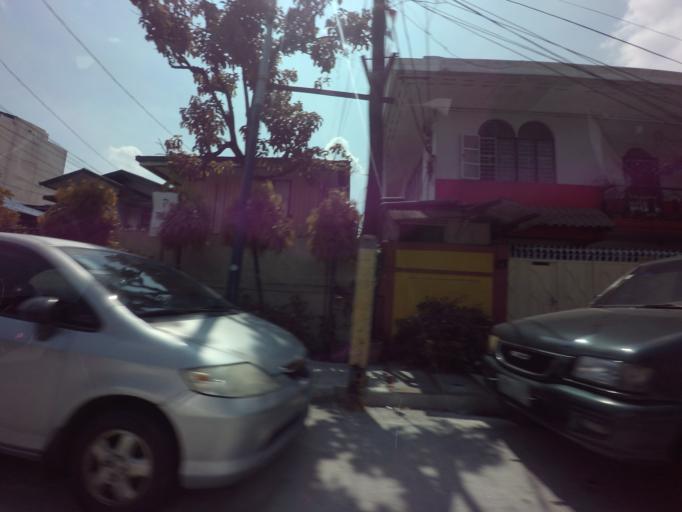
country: PH
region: Metro Manila
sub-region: Makati City
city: Makati City
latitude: 14.5656
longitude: 121.0089
